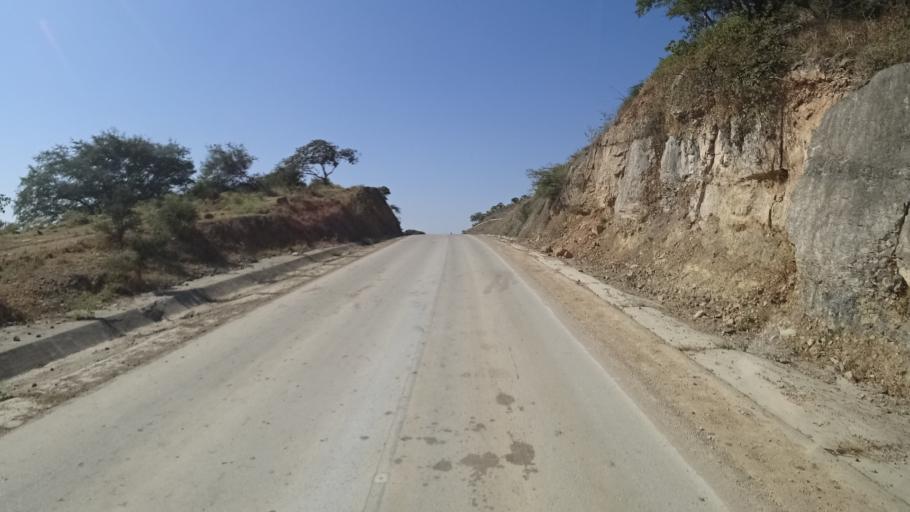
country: OM
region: Zufar
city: Salalah
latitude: 17.0620
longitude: 54.6055
